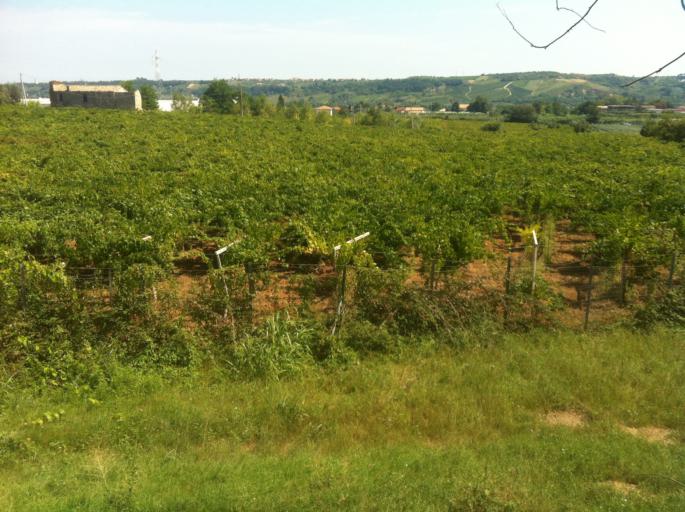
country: IT
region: Abruzzo
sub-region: Provincia di Chieti
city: Miglianico
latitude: 42.3879
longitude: 14.2901
